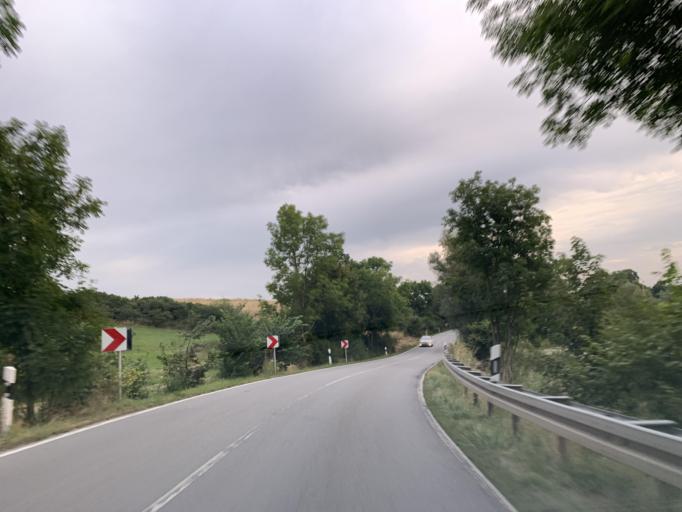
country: DE
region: Mecklenburg-Vorpommern
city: Neverin
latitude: 53.6008
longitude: 13.3281
